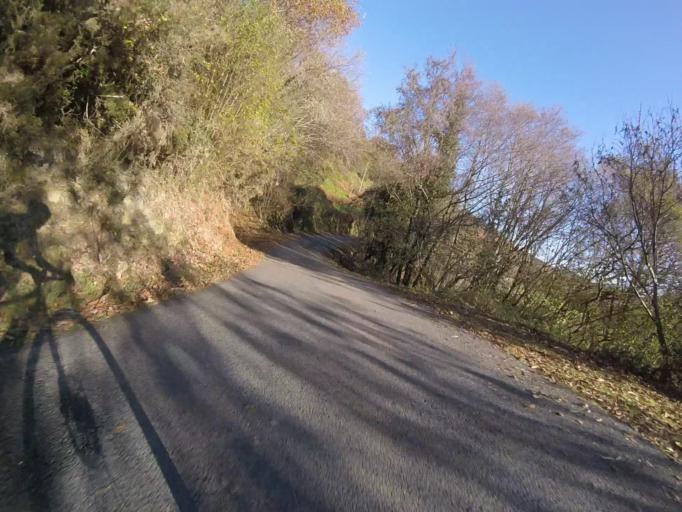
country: ES
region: Navarre
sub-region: Provincia de Navarra
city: Bera
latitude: 43.2971
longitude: -1.6555
